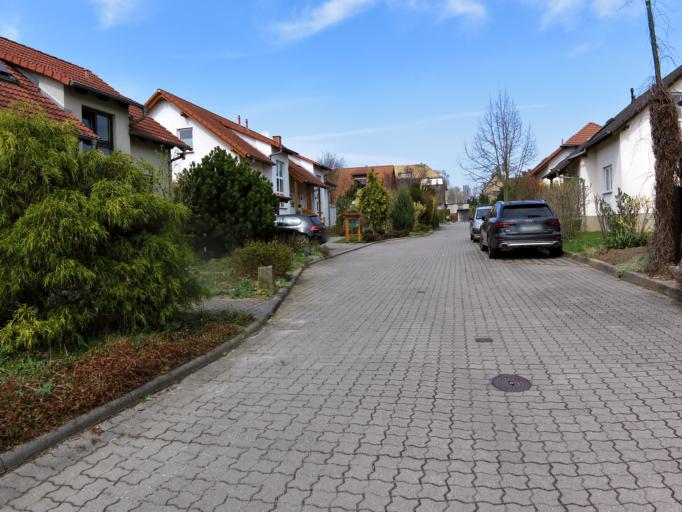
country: DE
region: Saxony
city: Schkeuditz
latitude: 51.3829
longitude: 12.2761
